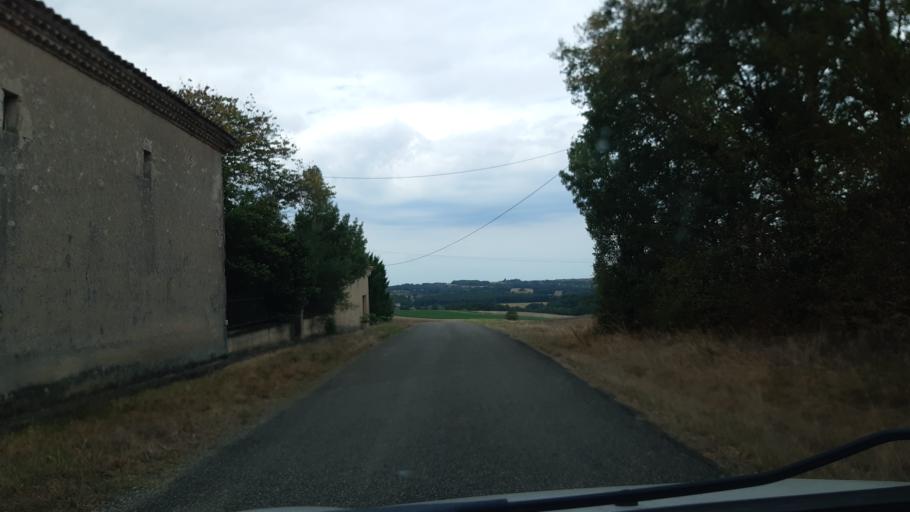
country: FR
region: Midi-Pyrenees
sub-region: Departement du Gers
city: Gimont
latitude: 43.7006
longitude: 0.9909
